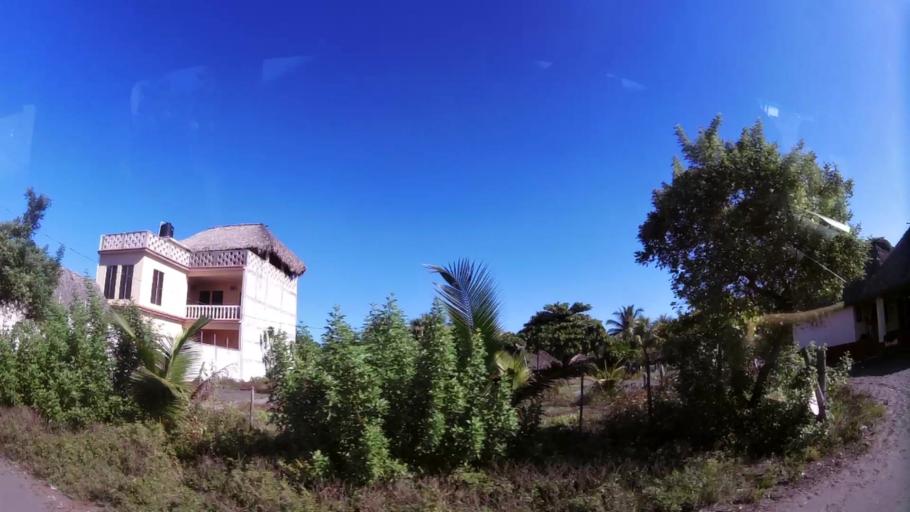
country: GT
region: Jutiapa
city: Pasaco
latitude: 13.8519
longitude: -90.3785
